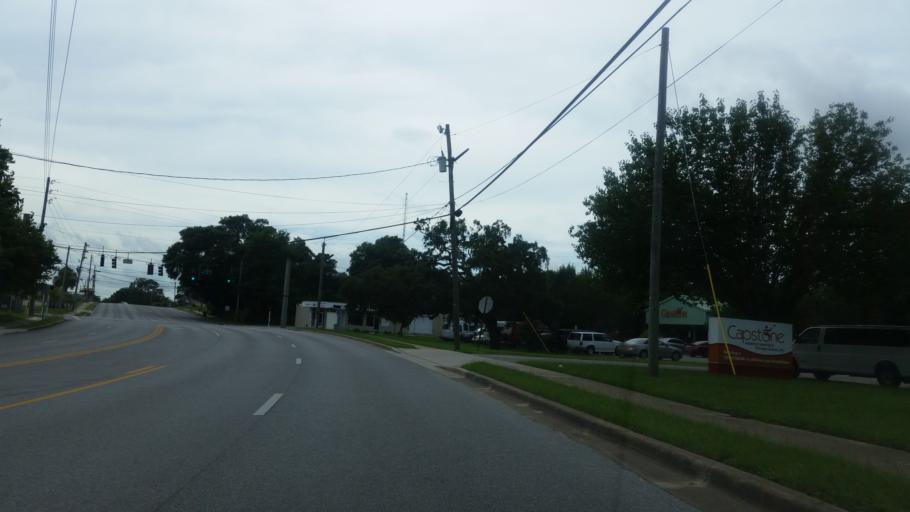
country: US
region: Florida
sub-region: Escambia County
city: Goulding
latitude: 30.4413
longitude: -87.2278
